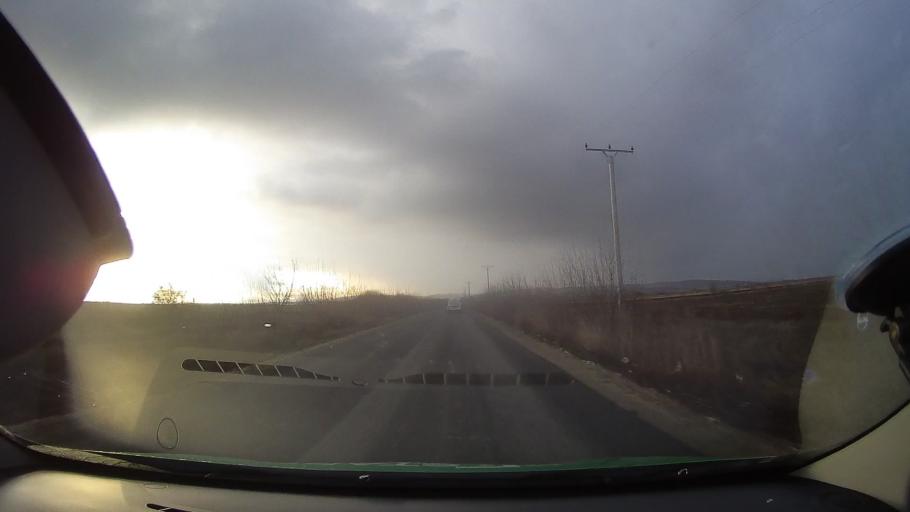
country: RO
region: Cluj
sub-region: Comuna Luna
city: Luncani
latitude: 46.4490
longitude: 23.9427
